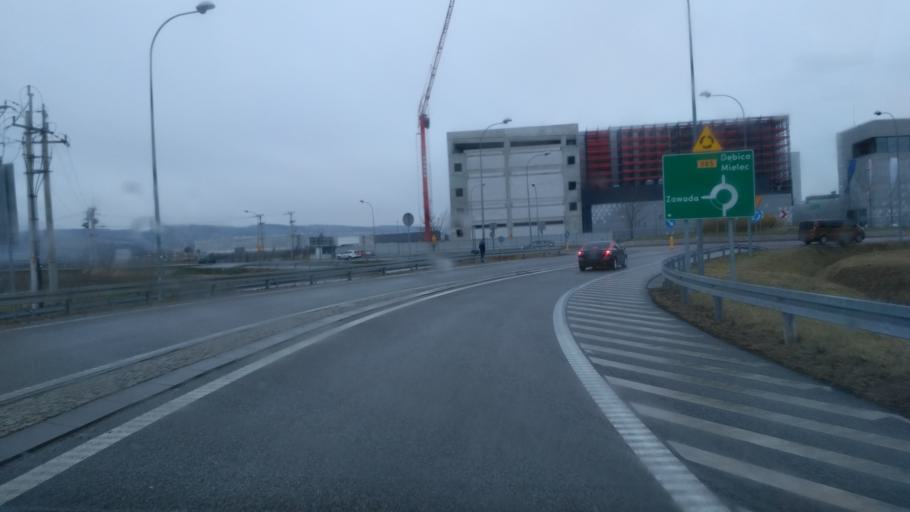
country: PL
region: Subcarpathian Voivodeship
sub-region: Powiat debicki
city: Brzeznica
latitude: 50.0757
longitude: 21.4690
